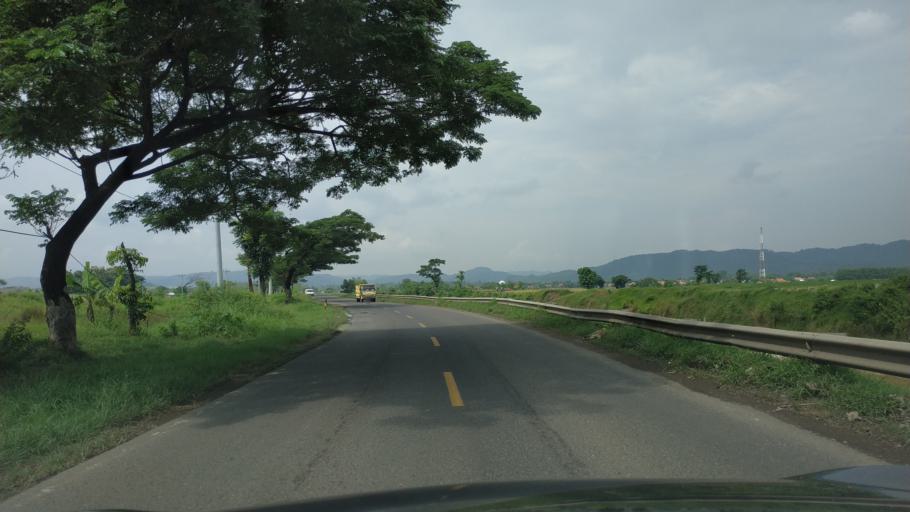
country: ID
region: Central Java
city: Margasari
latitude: -7.0814
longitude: 108.9824
